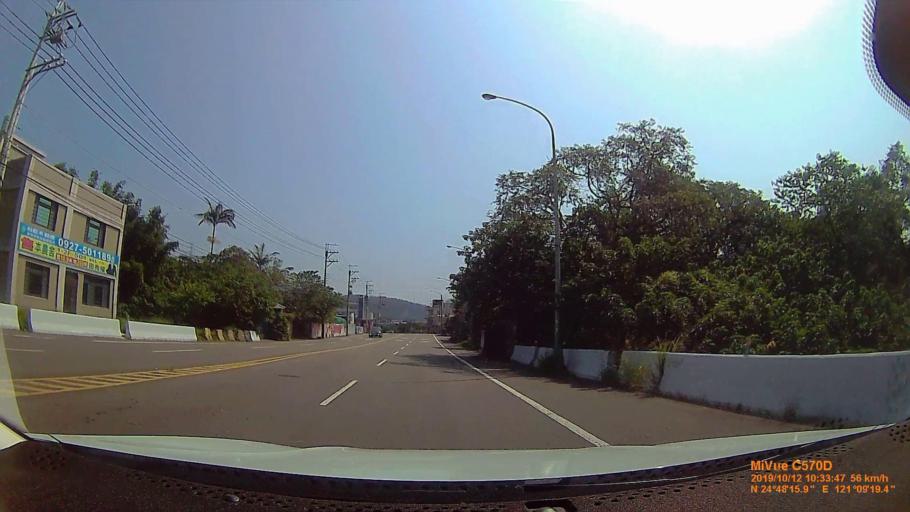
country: TW
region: Taiwan
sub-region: Hsinchu
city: Zhubei
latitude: 24.8042
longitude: 121.1557
